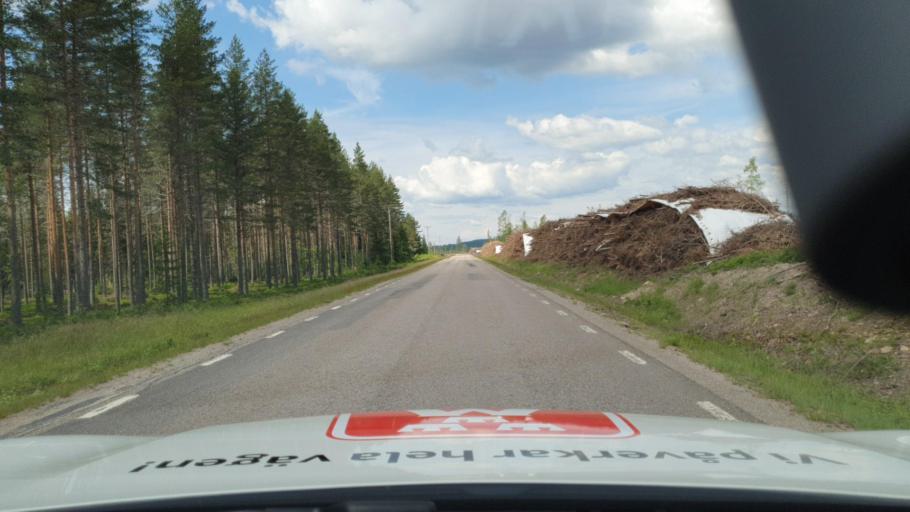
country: SE
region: Vaermland
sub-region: Torsby Kommun
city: Torsby
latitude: 60.5013
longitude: 12.8557
